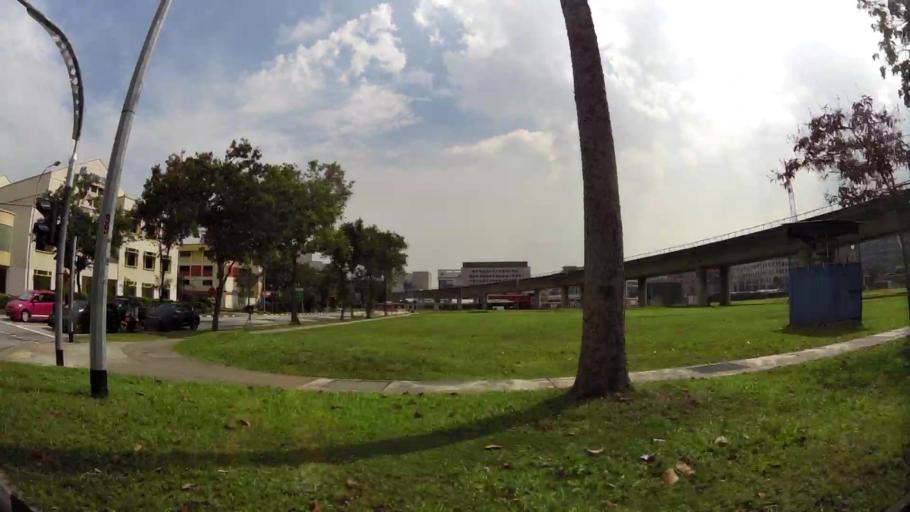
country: SG
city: Singapore
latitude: 1.3566
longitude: 103.9437
